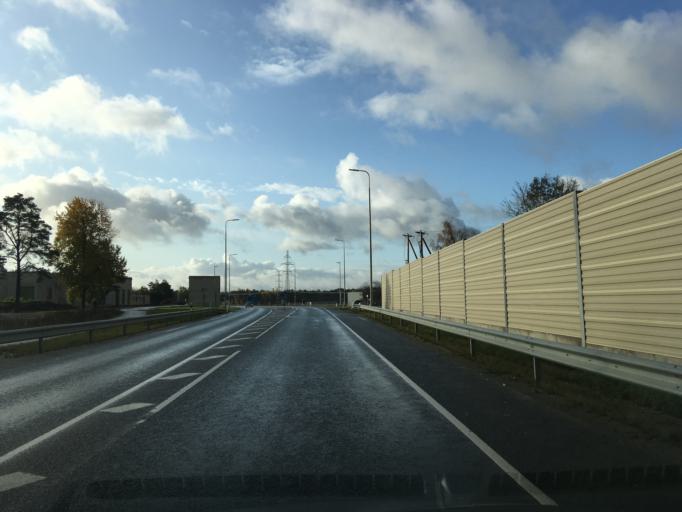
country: EE
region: Harju
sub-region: Saue vald
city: Laagri
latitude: 59.3506
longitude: 24.5990
